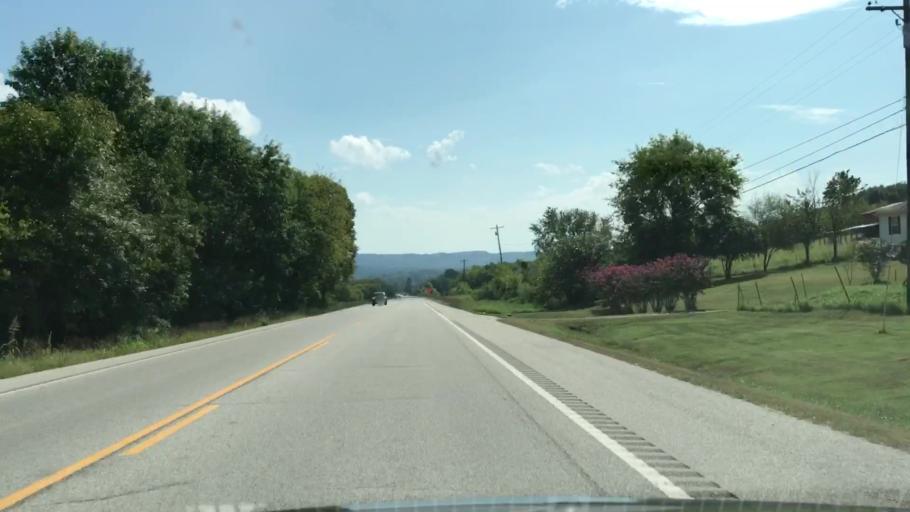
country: US
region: Tennessee
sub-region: Trousdale County
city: Hartsville
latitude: 36.3682
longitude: -86.0901
